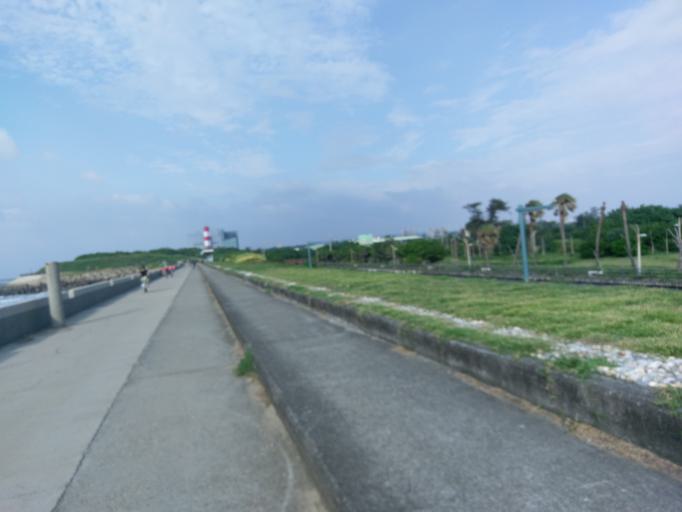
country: TW
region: Taiwan
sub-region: Hsinchu
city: Hsinchu
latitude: 24.8256
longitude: 120.9109
